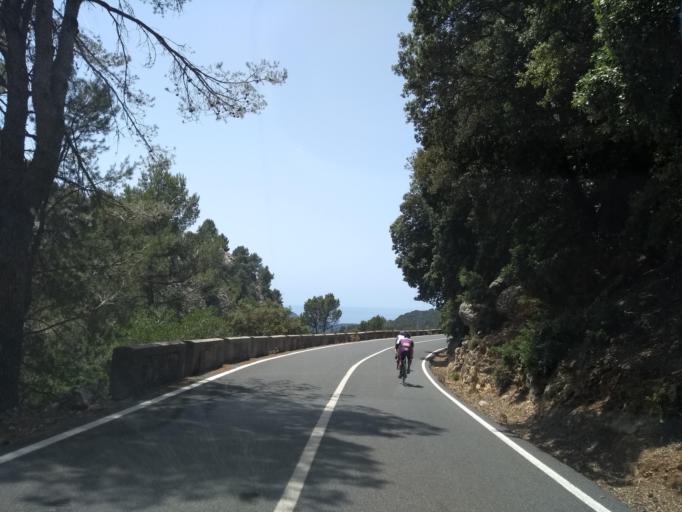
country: ES
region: Balearic Islands
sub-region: Illes Balears
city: Fornalutx
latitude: 39.7954
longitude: 2.7632
